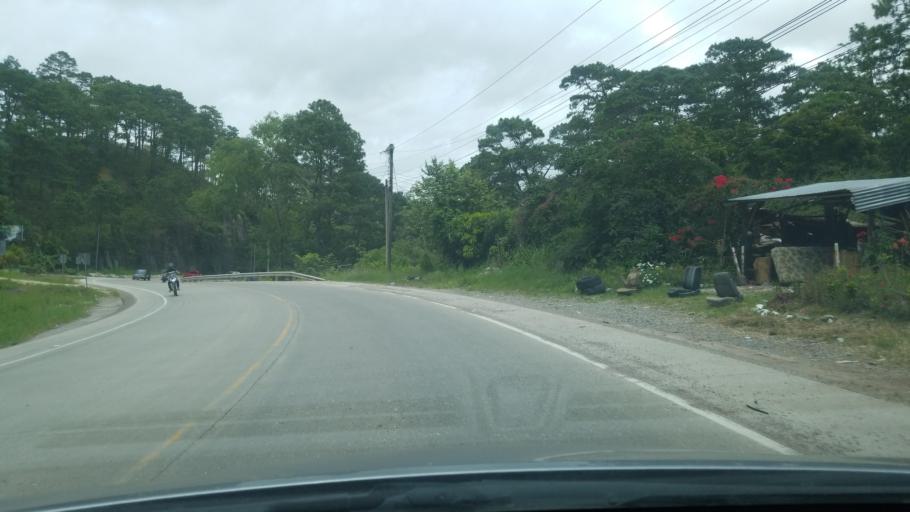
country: HN
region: Copan
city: Santa Rosa de Copan
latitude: 14.8040
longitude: -88.7747
